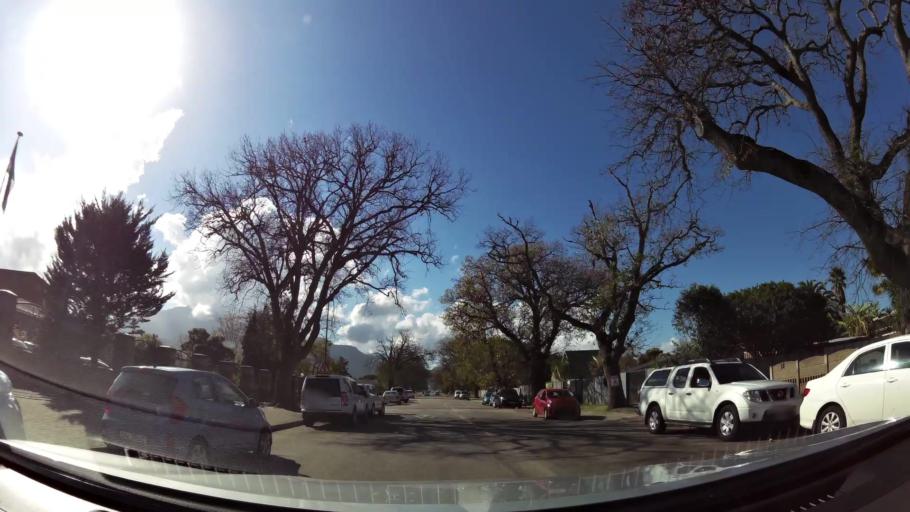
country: ZA
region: Western Cape
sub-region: Eden District Municipality
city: George
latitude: -33.9709
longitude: 22.4516
